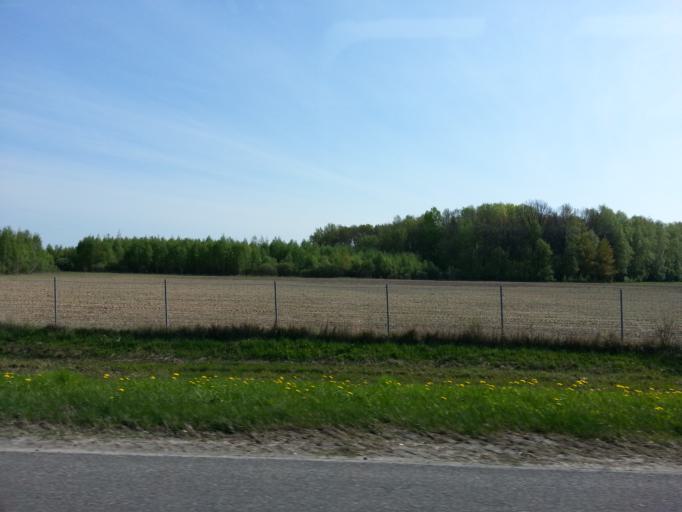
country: LT
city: Sirvintos
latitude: 54.9835
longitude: 24.9367
